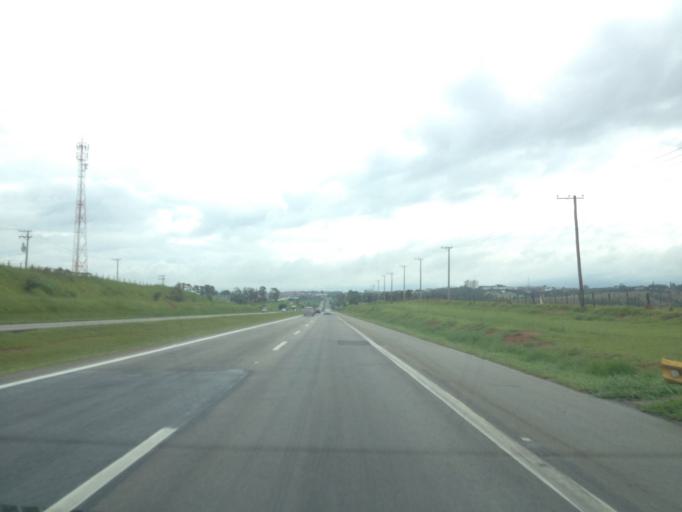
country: BR
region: Sao Paulo
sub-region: Itu
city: Itu
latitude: -23.2880
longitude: -47.3295
